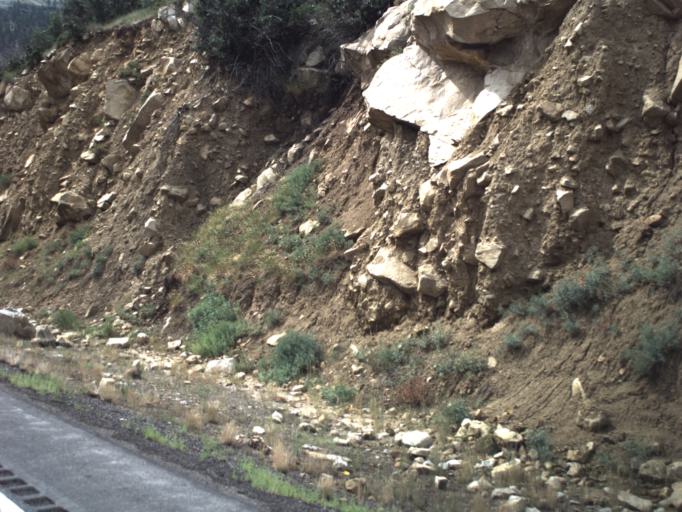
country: US
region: Utah
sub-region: Carbon County
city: Helper
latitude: 39.7662
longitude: -110.9049
